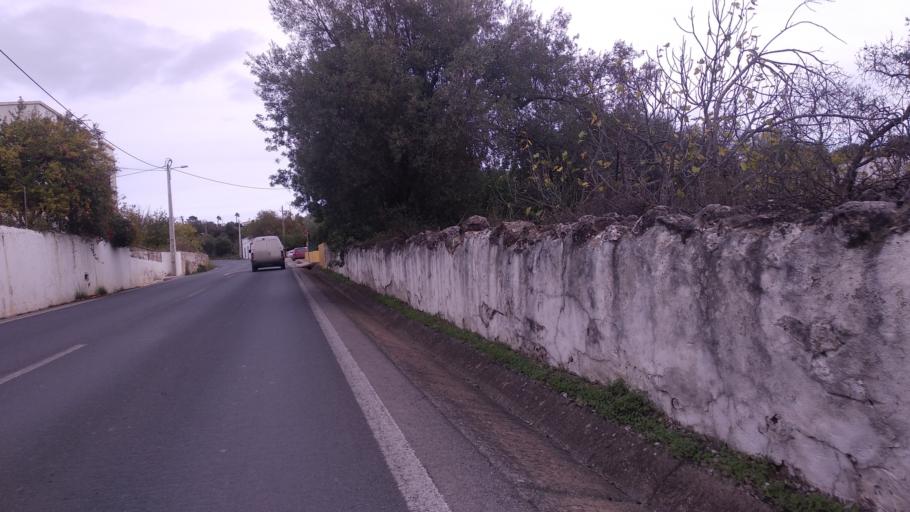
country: PT
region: Faro
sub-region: Loule
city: Loule
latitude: 37.1387
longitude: -7.9900
